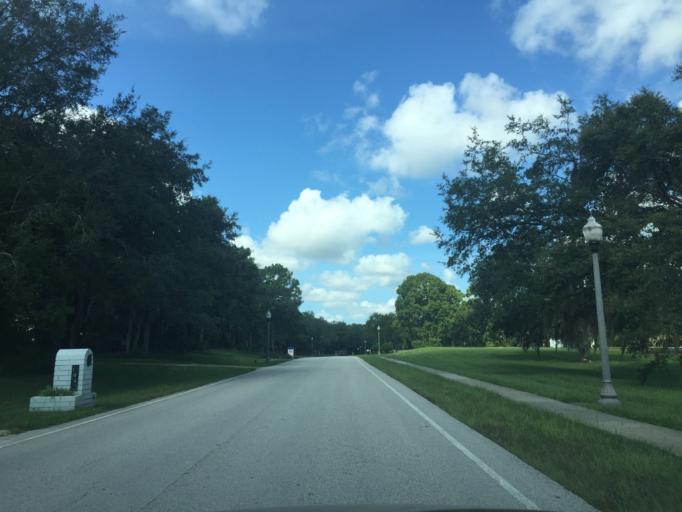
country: US
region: Florida
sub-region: Seminole County
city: Oviedo
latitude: 28.6652
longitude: -81.2537
